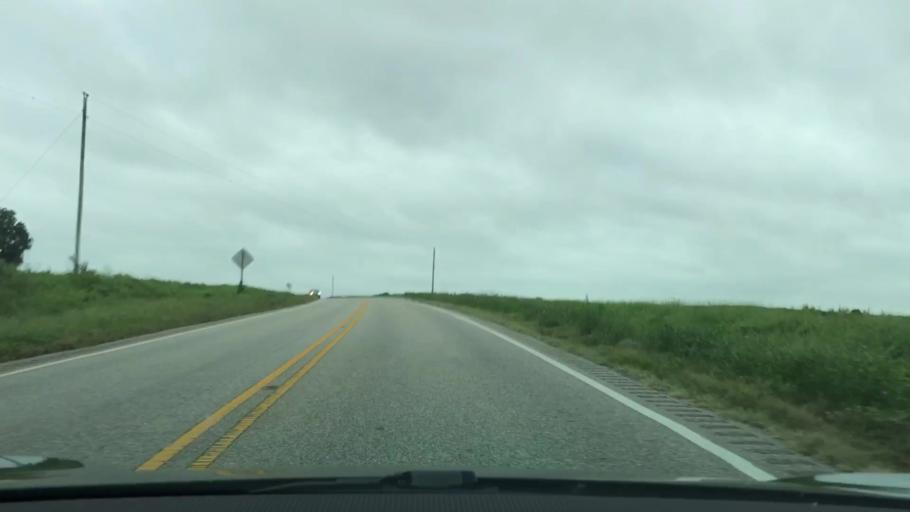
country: US
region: Alabama
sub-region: Covington County
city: Opp
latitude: 31.2864
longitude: -86.1496
